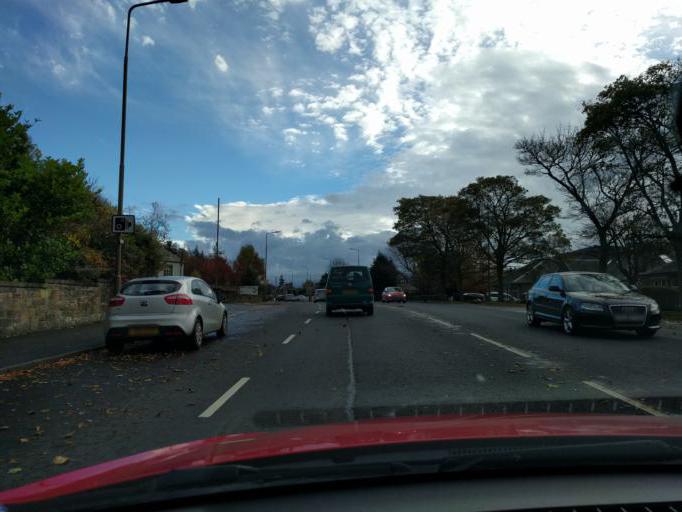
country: GB
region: Scotland
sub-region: Edinburgh
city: Edinburgh
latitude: 55.9053
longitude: -3.2079
